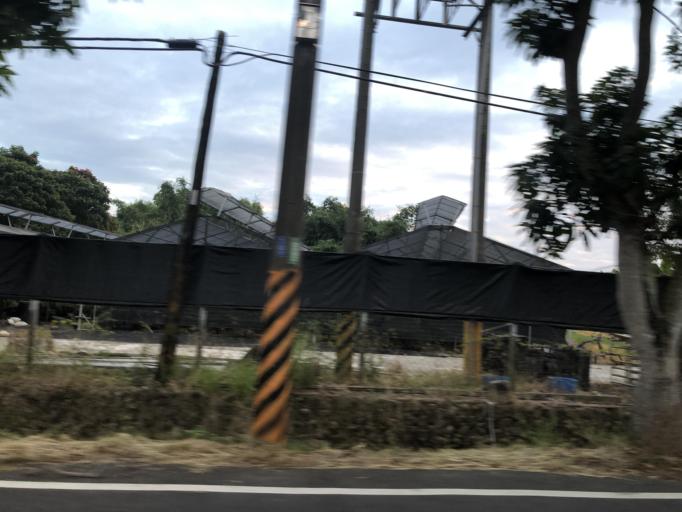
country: TW
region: Taiwan
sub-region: Tainan
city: Tainan
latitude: 23.0257
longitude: 120.3447
